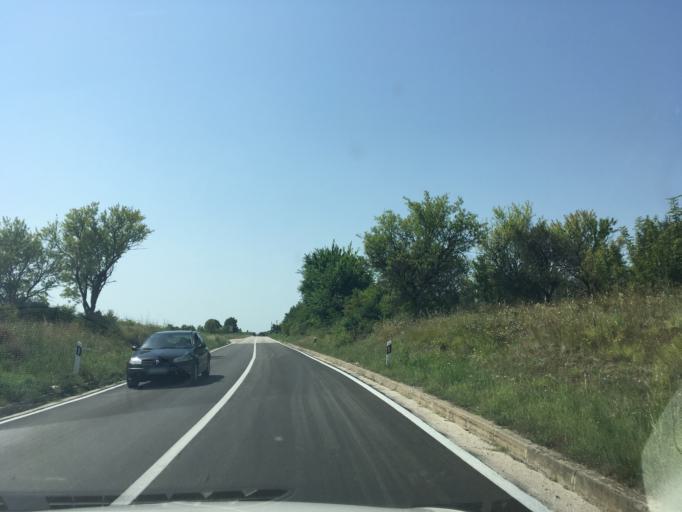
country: HR
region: Zadarska
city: Benkovac
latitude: 44.0180
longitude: 15.6426
